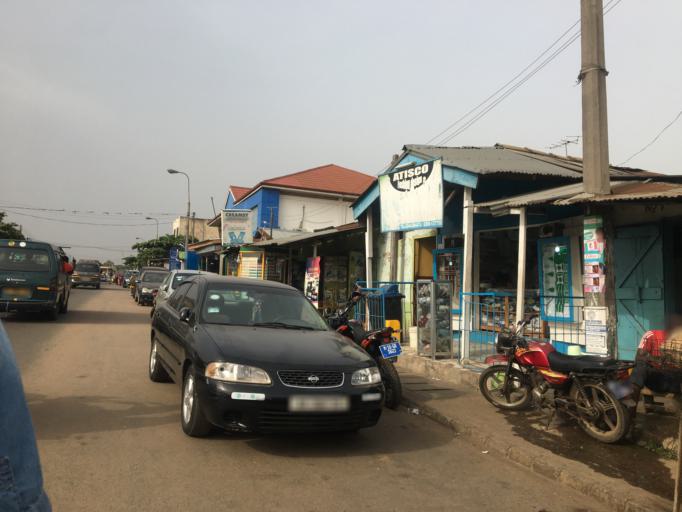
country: GH
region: Greater Accra
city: Accra
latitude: 5.5913
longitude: -0.1957
